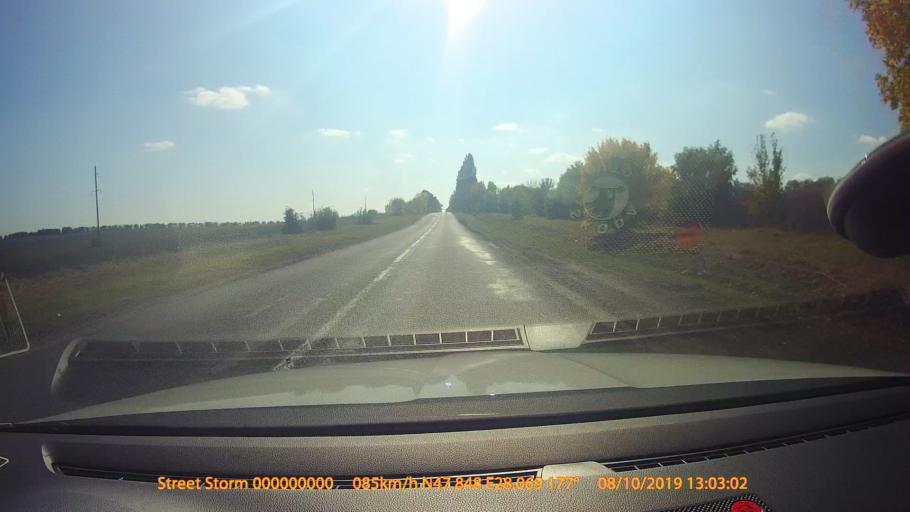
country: MD
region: Singerei
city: Biruinta
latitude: 47.8475
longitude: 28.0693
